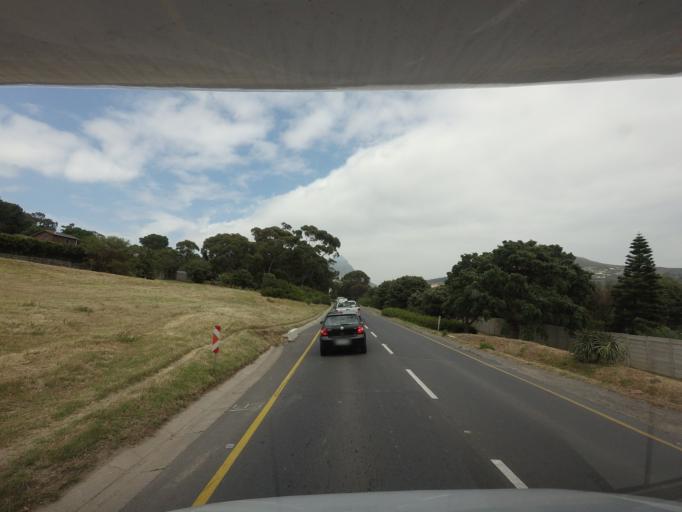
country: ZA
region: Western Cape
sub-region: City of Cape Town
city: Constantia
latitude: -34.0217
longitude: 18.3674
